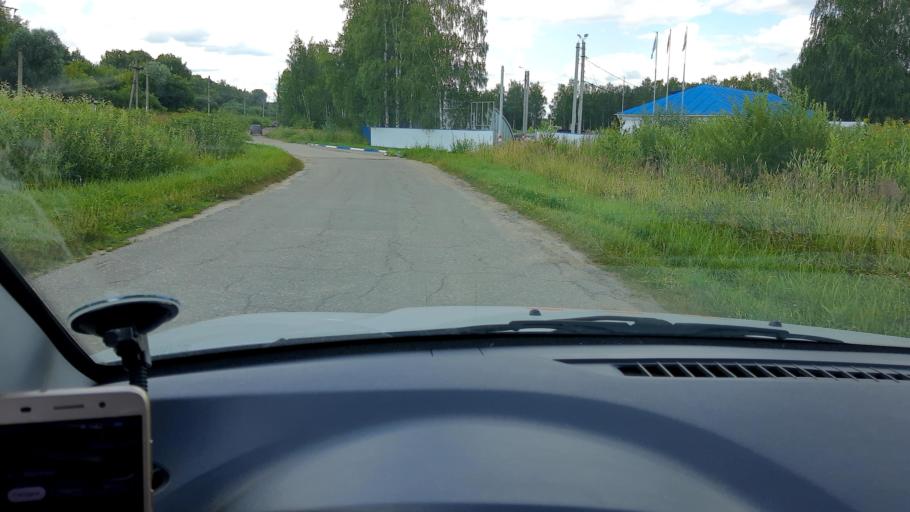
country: RU
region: Nizjnij Novgorod
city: Afonino
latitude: 56.2018
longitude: 44.0314
